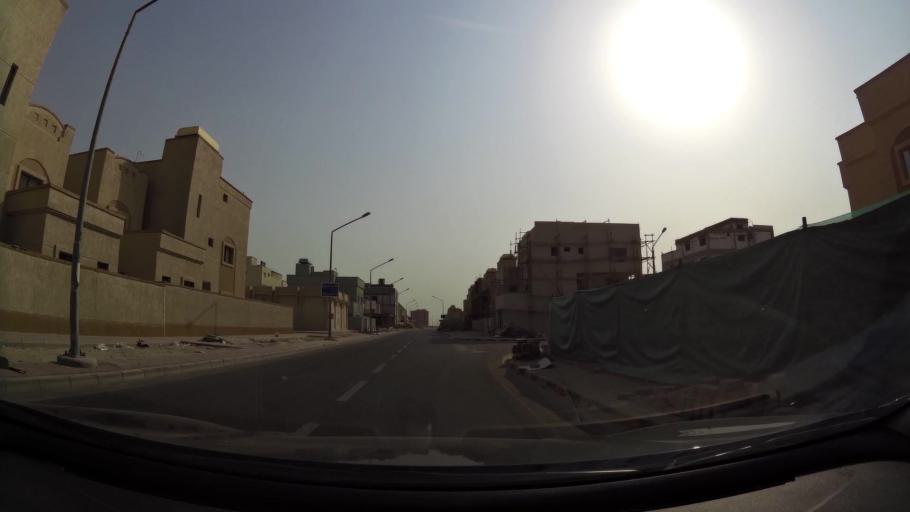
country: KW
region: Al Asimah
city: Ar Rabiyah
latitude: 29.3333
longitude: 47.8061
